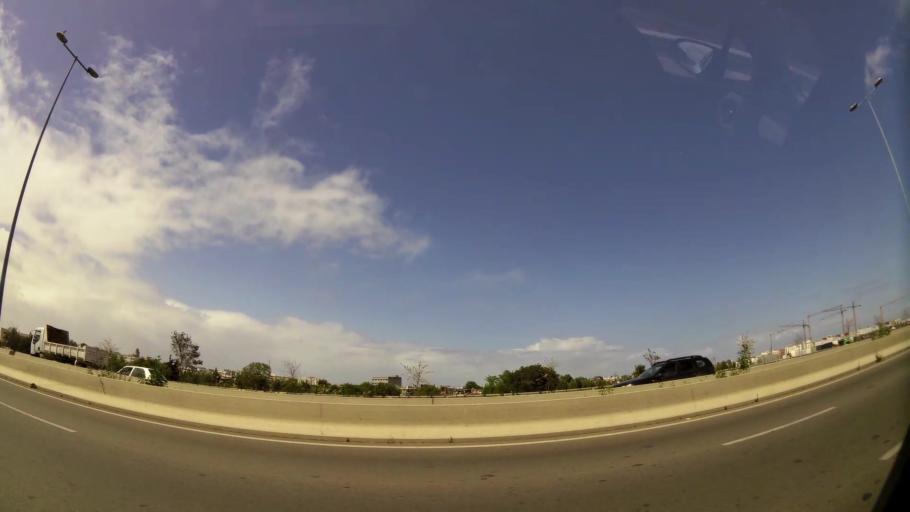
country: MA
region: Grand Casablanca
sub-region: Mediouna
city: Tit Mellil
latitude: 33.5967
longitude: -7.5154
